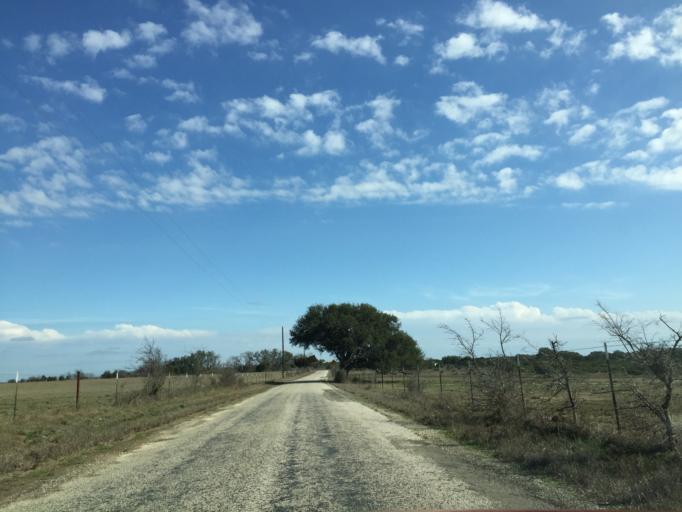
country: US
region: Texas
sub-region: Williamson County
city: Florence
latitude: 30.7819
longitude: -97.8941
